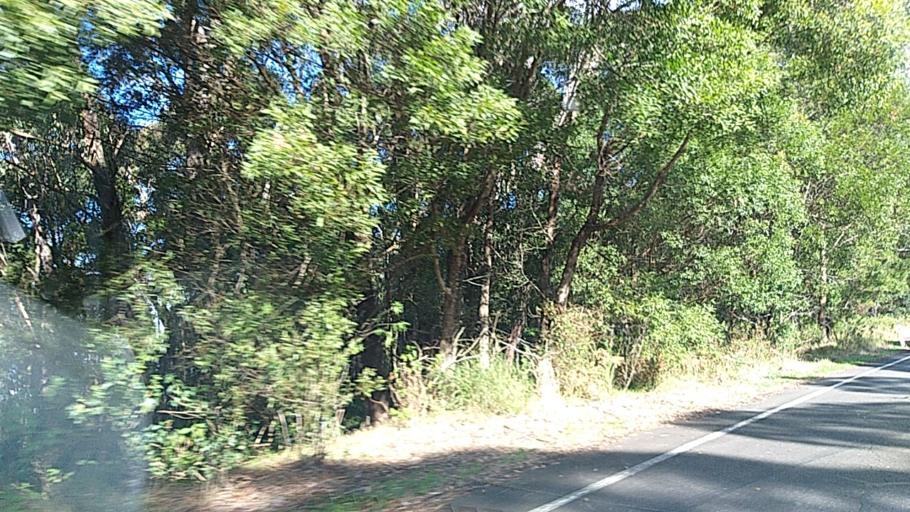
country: AU
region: New South Wales
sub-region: Wollongong
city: Mount Keira
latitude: -34.3998
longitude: 150.8418
